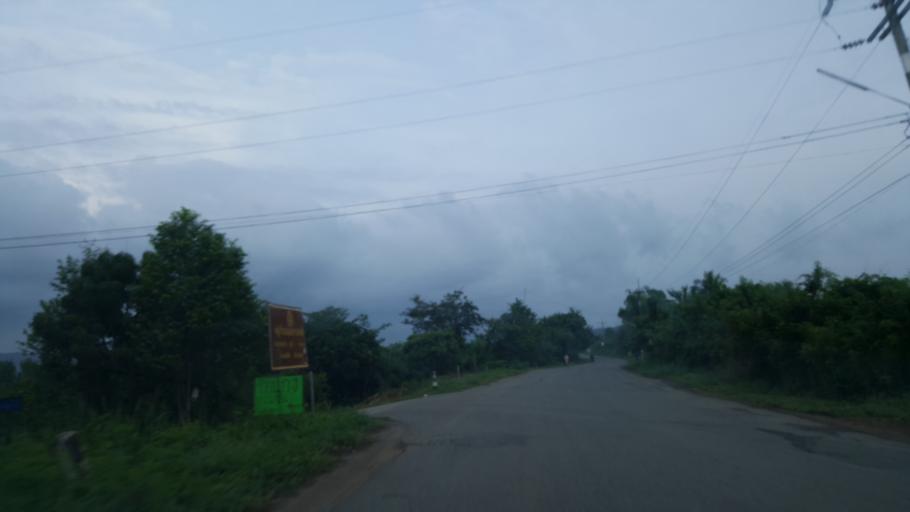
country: TH
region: Chon Buri
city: Sattahip
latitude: 12.7188
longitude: 100.9181
